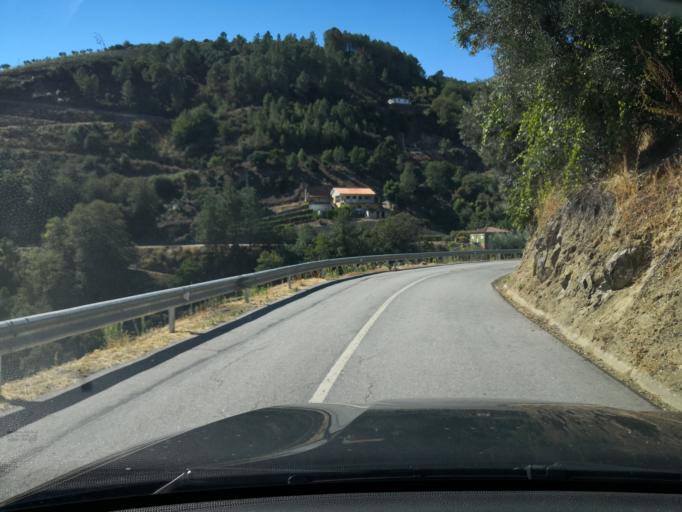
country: PT
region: Vila Real
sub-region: Santa Marta de Penaguiao
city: Santa Marta de Penaguiao
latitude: 41.2319
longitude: -7.7921
